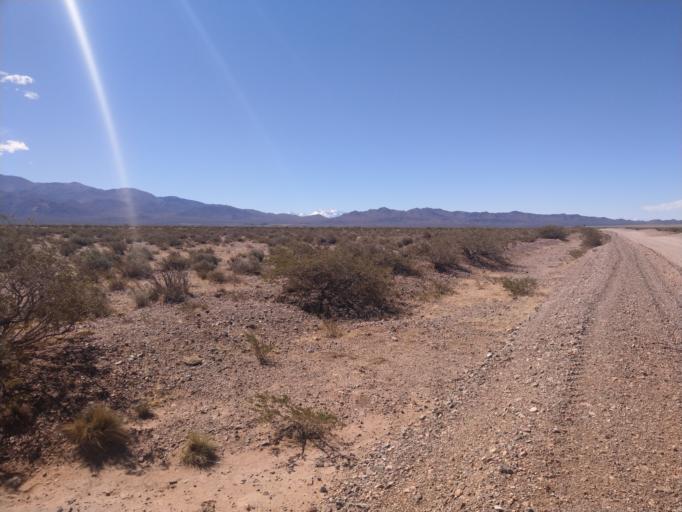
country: AR
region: San Juan
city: Tamberias
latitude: -32.1665
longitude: -69.3439
